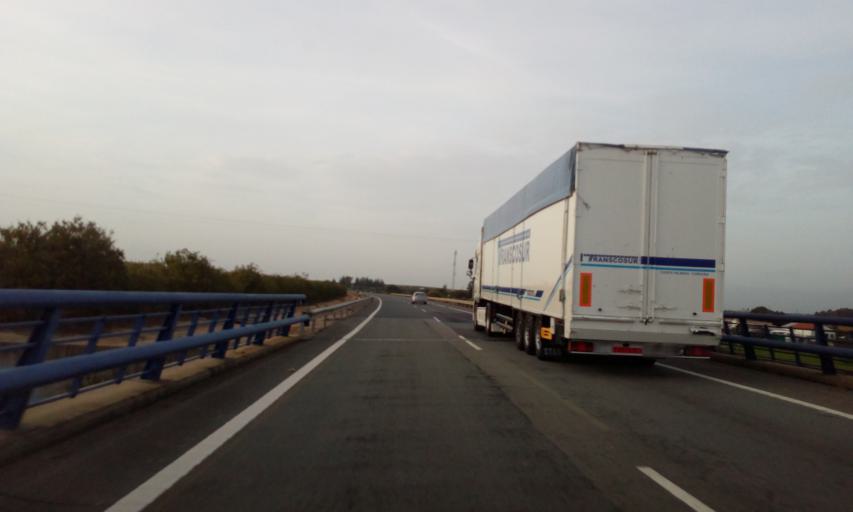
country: ES
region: Andalusia
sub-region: Provincia de Huelva
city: Gibraleon
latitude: 37.3504
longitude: -6.9291
